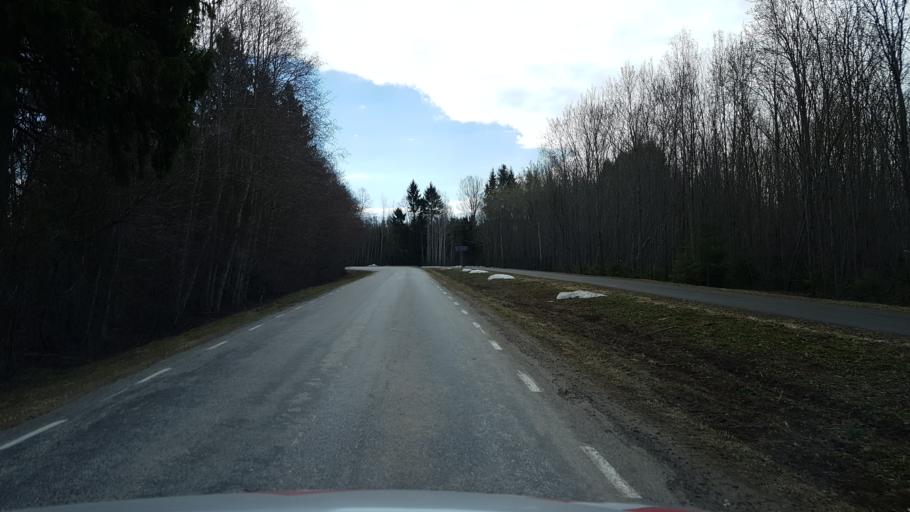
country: EE
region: Laeaene-Virumaa
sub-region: Haljala vald
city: Haljala
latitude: 59.3923
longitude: 26.2904
